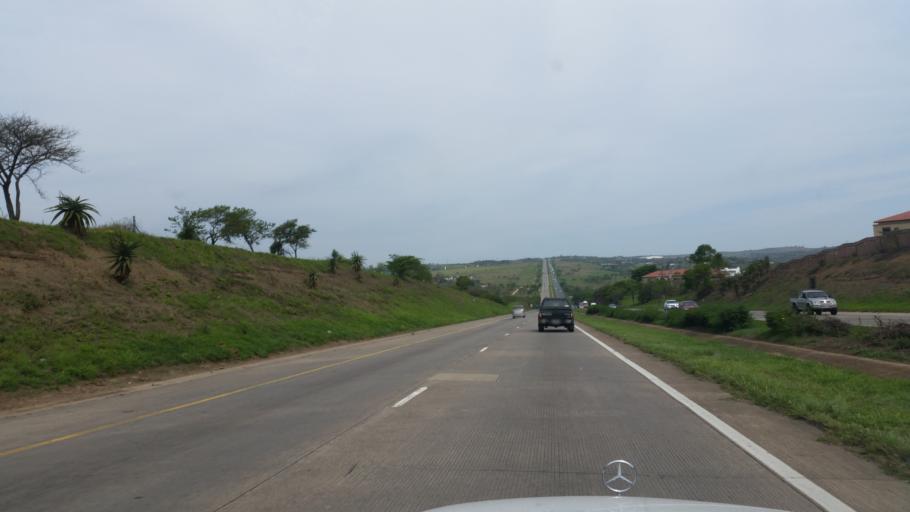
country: ZA
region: KwaZulu-Natal
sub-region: uMgungundlovu District Municipality
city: Pietermaritzburg
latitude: -29.6628
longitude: 30.4579
